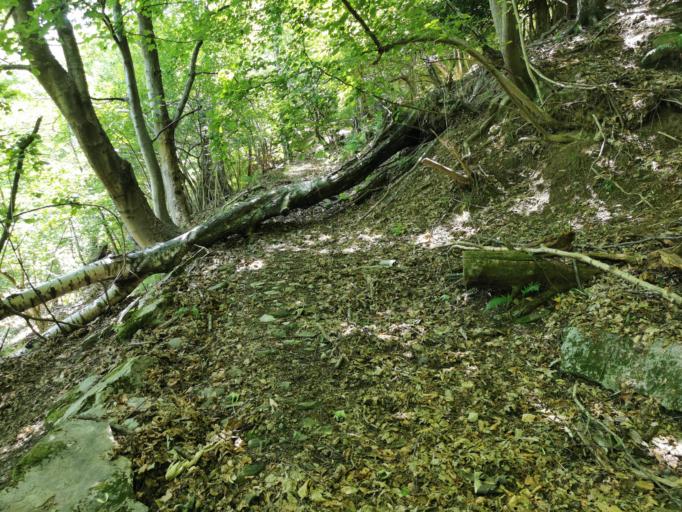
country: IT
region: Lombardy
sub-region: Provincia di Como
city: Torno
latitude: 45.8449
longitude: 9.1351
